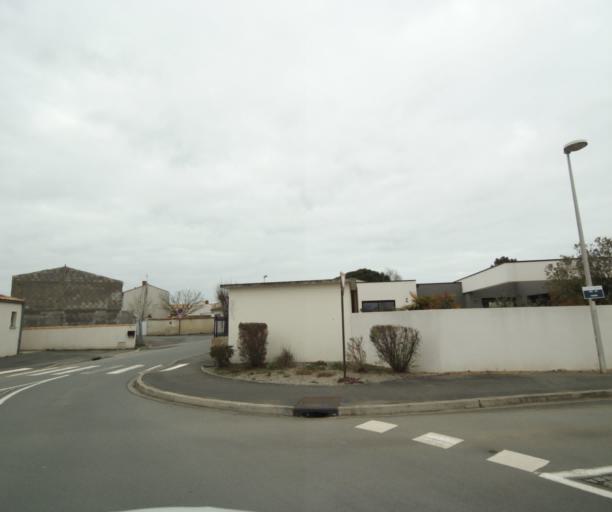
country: FR
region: Poitou-Charentes
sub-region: Departement de la Charente-Maritime
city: Lagord
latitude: 46.1918
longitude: -1.1513
